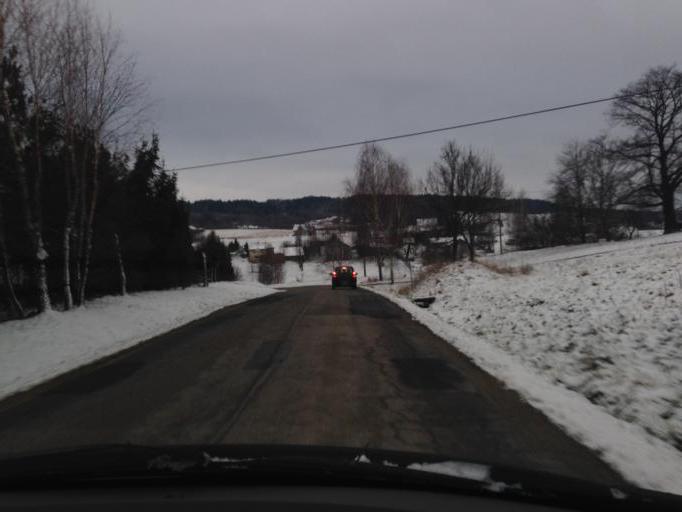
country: PL
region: Lesser Poland Voivodeship
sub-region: Powiat gorlicki
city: Moszczenica
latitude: 49.7460
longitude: 21.0840
